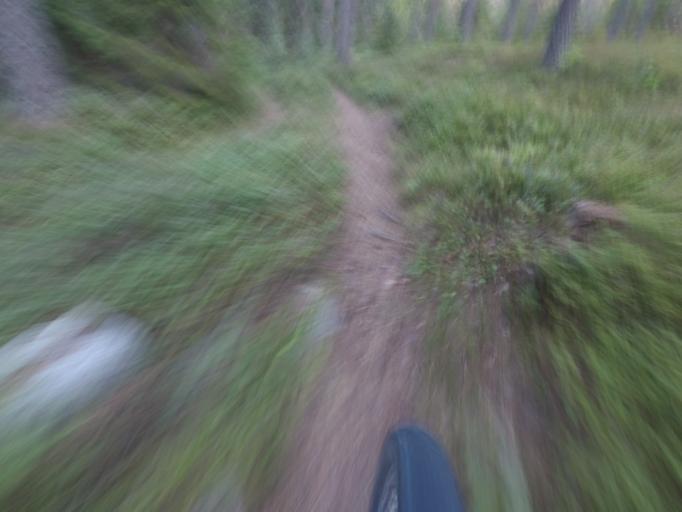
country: SE
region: Soedermanland
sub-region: Eskilstuna Kommun
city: Kvicksund
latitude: 59.4140
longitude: 16.3175
